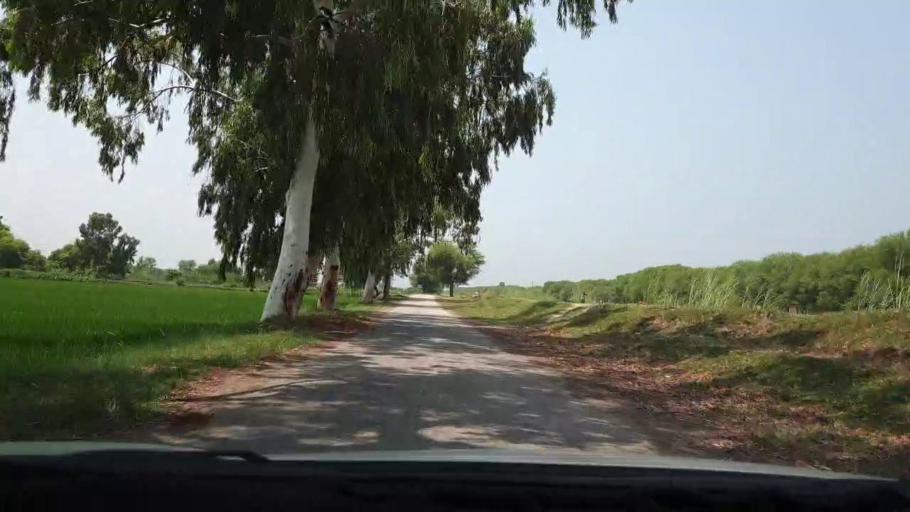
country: PK
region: Sindh
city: Dokri
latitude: 27.3132
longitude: 68.1019
